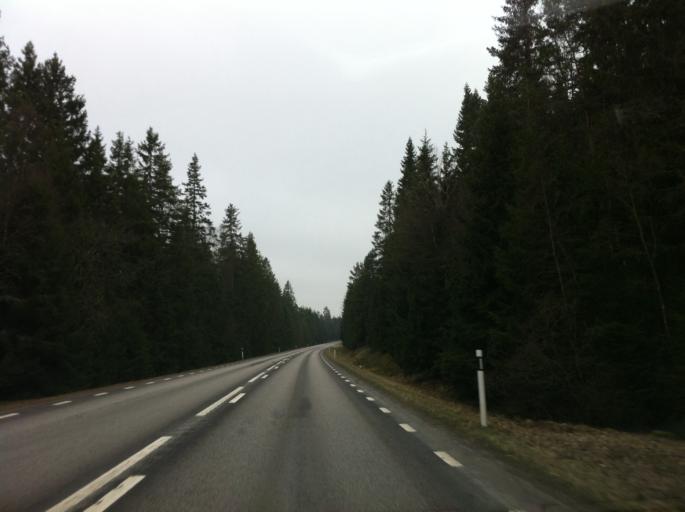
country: SE
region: Vaestra Goetaland
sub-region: Boras Kommun
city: Ganghester
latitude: 57.6617
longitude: 13.0592
